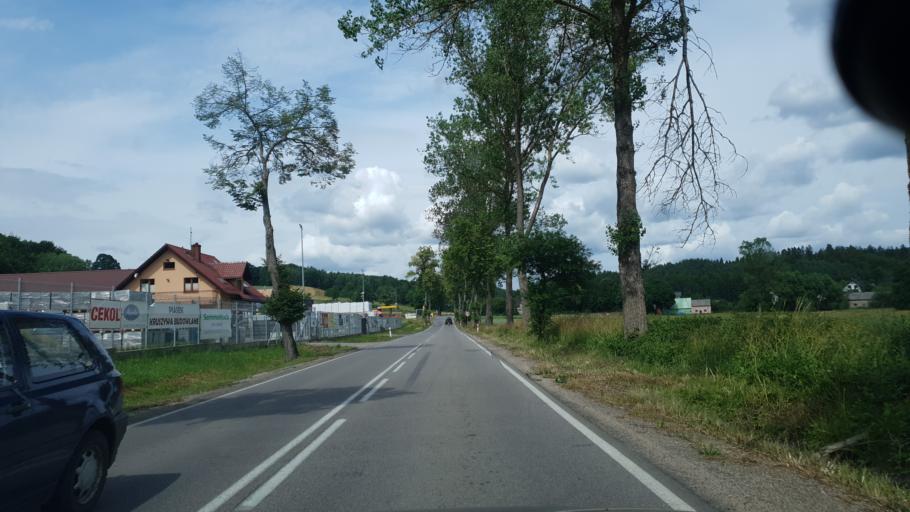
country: PL
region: Pomeranian Voivodeship
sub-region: Powiat kartuski
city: Chmielno
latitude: 54.3015
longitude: 18.1449
